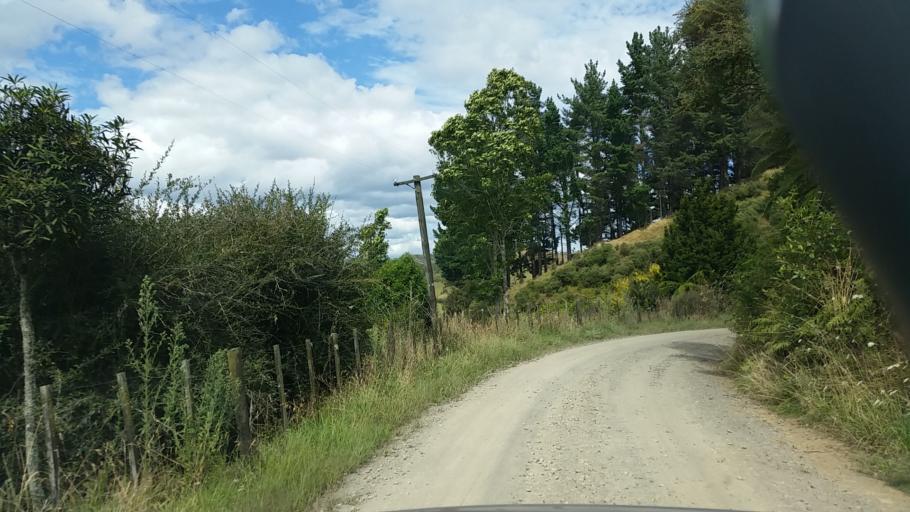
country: NZ
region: Taranaki
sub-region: South Taranaki District
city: Eltham
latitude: -39.2511
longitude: 174.5657
